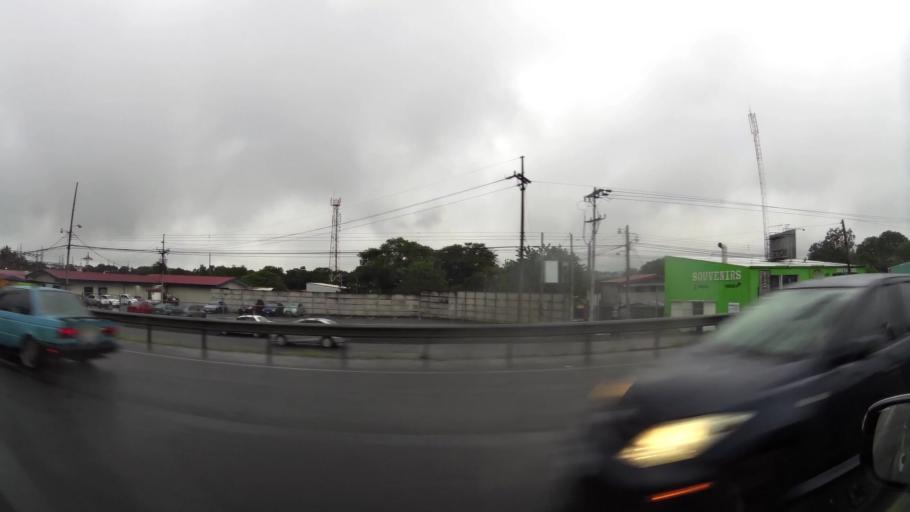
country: CR
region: Alajuela
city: Alajuela
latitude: 9.9981
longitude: -84.2237
